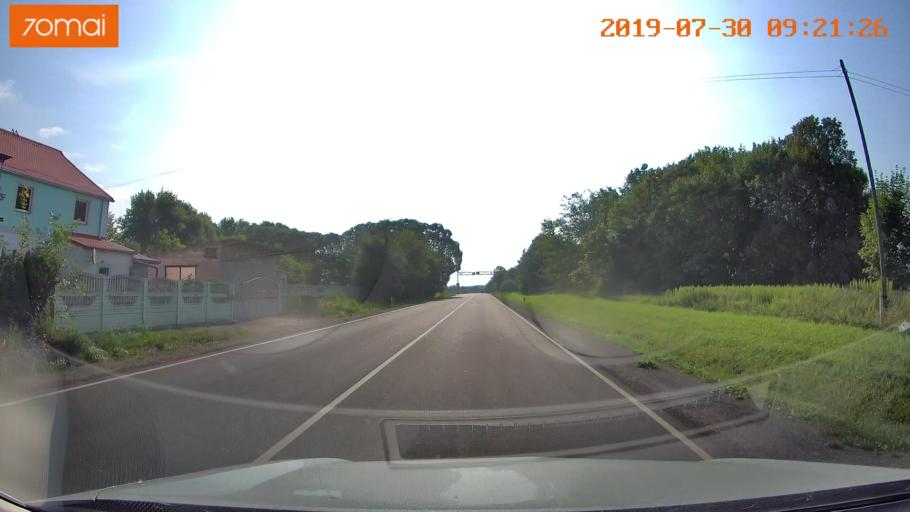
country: RU
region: Kaliningrad
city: Nesterov
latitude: 54.6355
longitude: 22.6314
